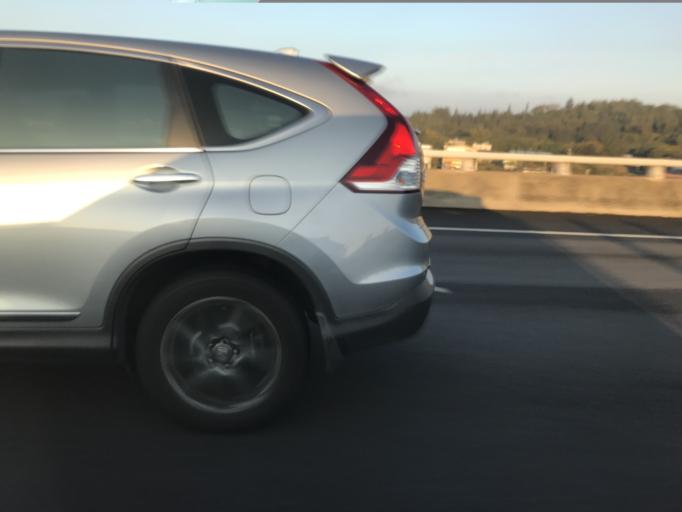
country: TW
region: Taiwan
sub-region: Miaoli
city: Miaoli
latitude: 24.6214
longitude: 120.8128
